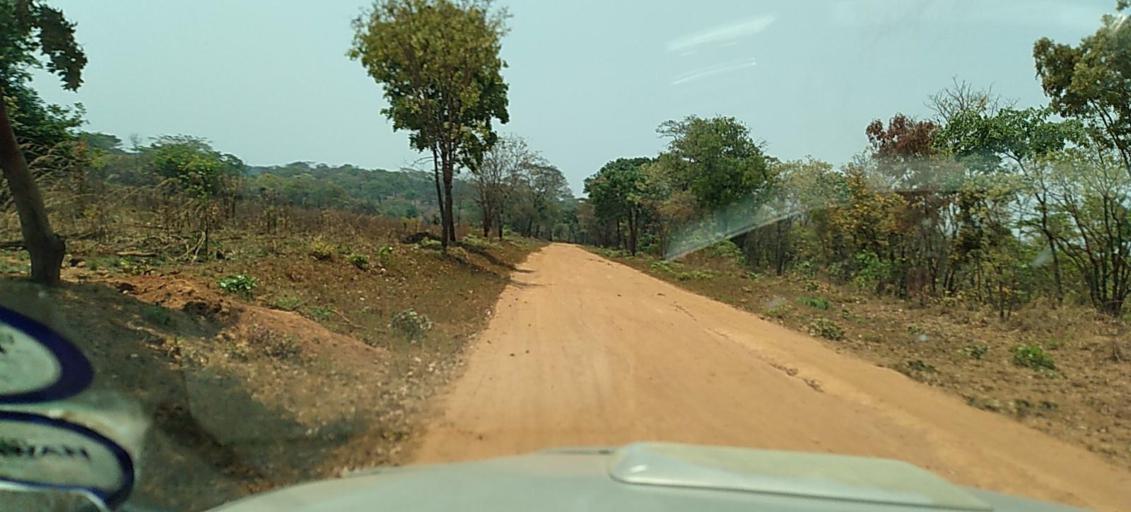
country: ZM
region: North-Western
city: Kasempa
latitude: -13.5458
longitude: 26.0387
